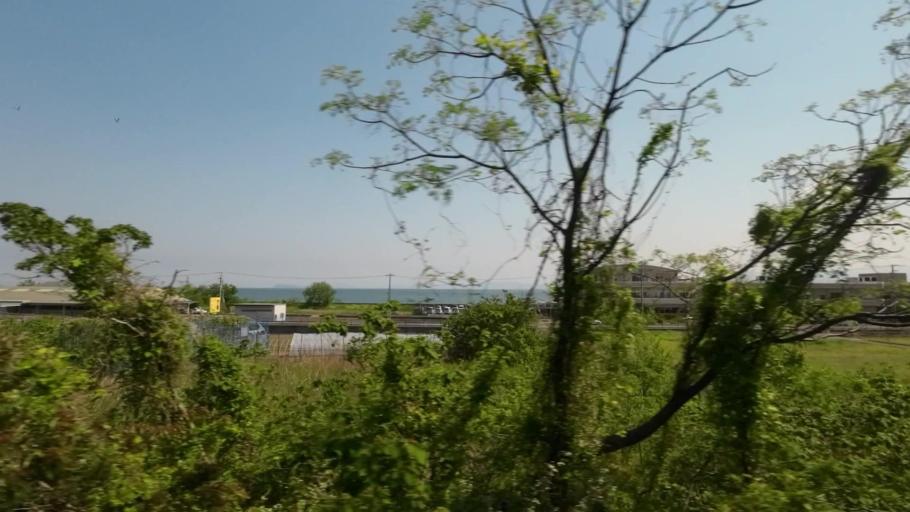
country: JP
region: Ehime
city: Kawanoecho
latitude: 33.9692
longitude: 133.4861
